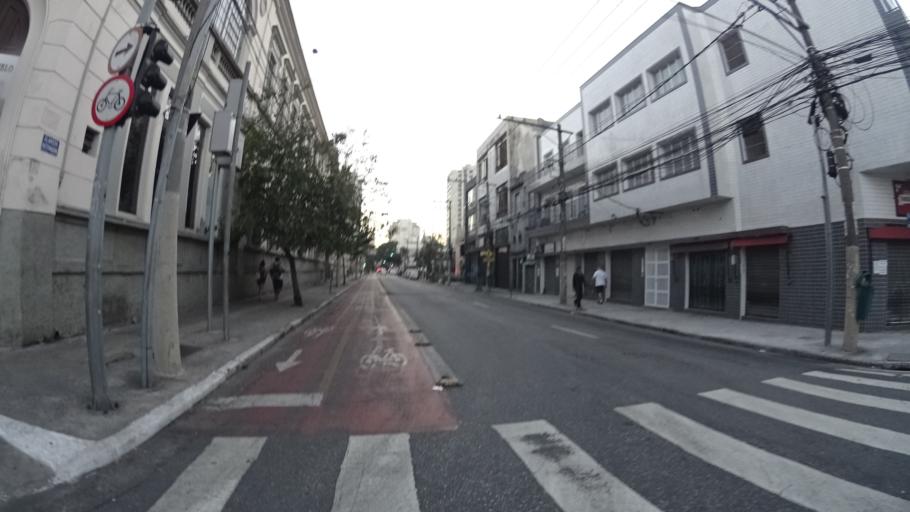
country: BR
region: Sao Paulo
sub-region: Sao Paulo
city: Sao Paulo
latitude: -23.5312
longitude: -46.6439
